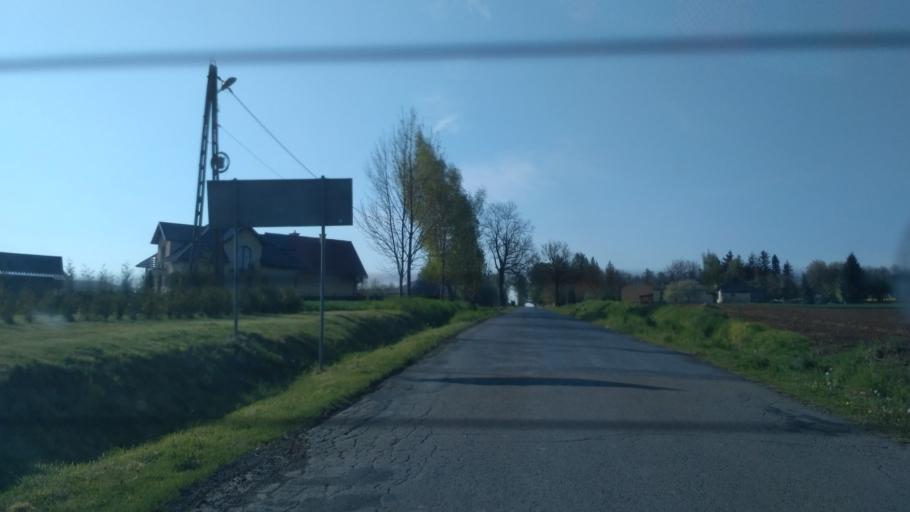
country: PL
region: Subcarpathian Voivodeship
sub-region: Powiat jaroslawski
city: Pruchnik
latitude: 49.9029
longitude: 22.5492
